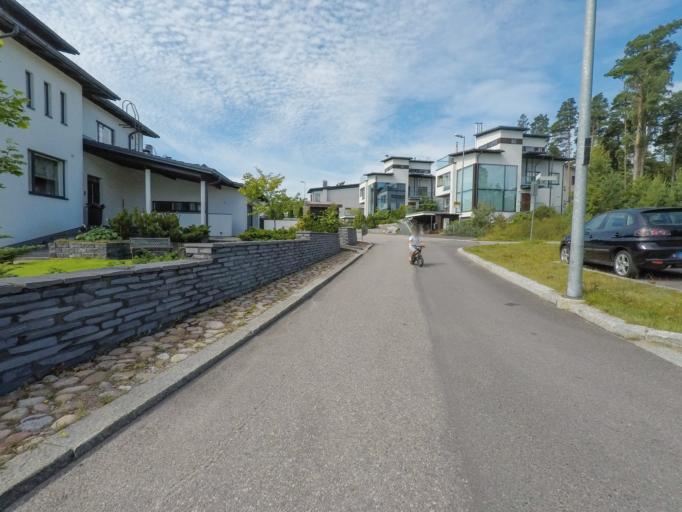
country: FI
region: Uusimaa
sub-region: Helsinki
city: Vantaa
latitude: 60.1609
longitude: 25.0931
